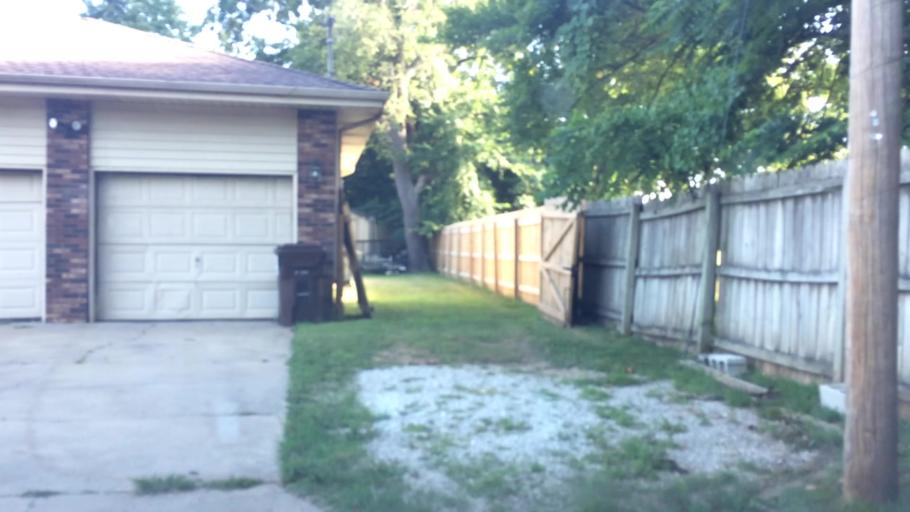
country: US
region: Missouri
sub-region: Greene County
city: Springfield
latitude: 37.2608
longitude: -93.2785
